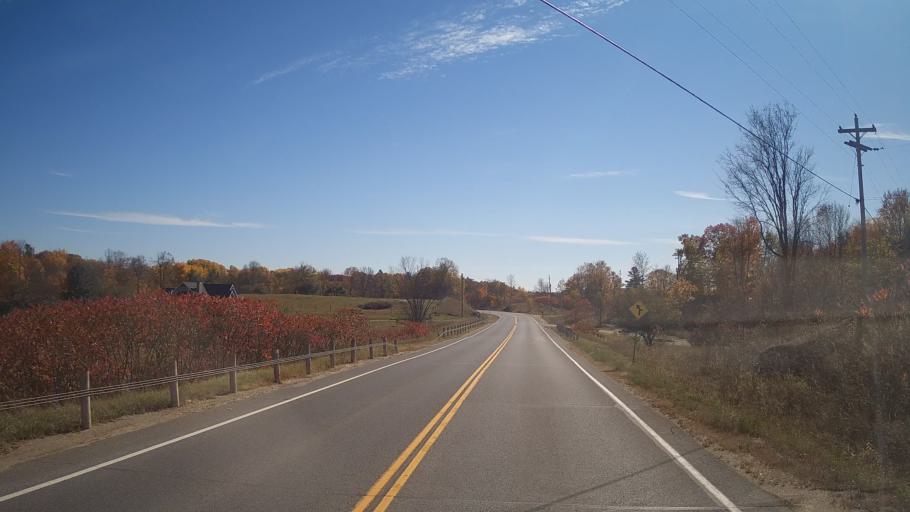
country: CA
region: Ontario
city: Perth
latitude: 44.6809
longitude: -76.6722
